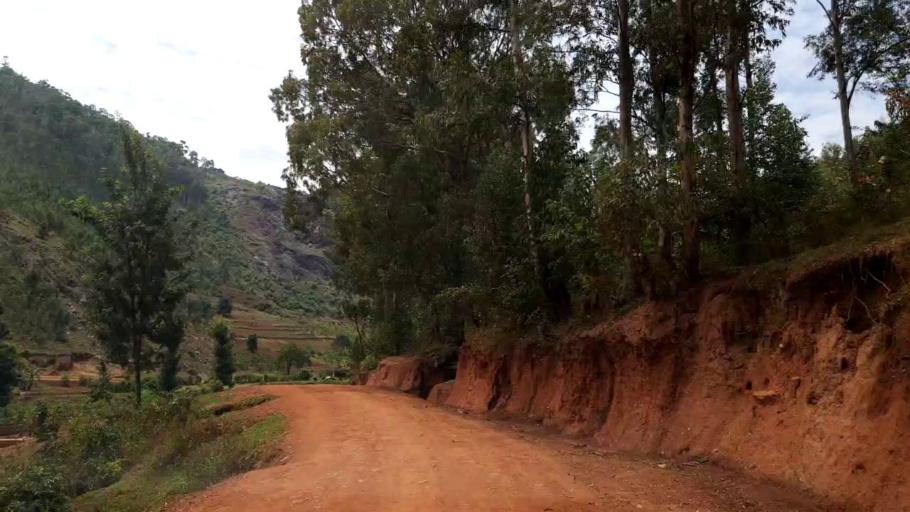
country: RW
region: Northern Province
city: Byumba
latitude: -1.5119
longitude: 30.1935
